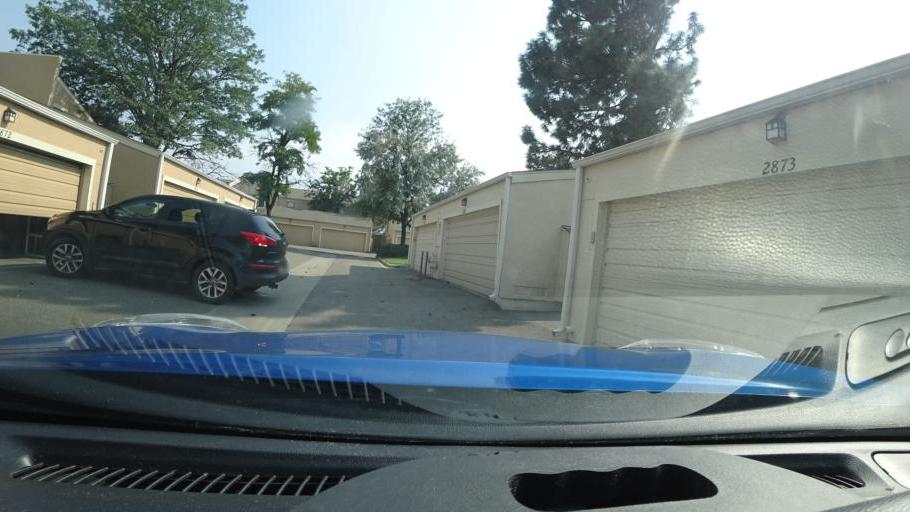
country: US
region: Colorado
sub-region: Adams County
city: Aurora
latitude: 39.6647
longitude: -104.8363
